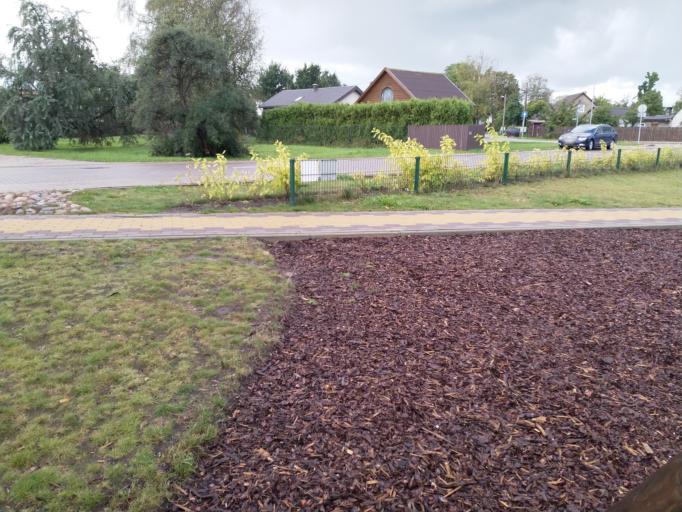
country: LV
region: Ventspils
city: Ventspils
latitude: 57.3741
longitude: 21.5892
